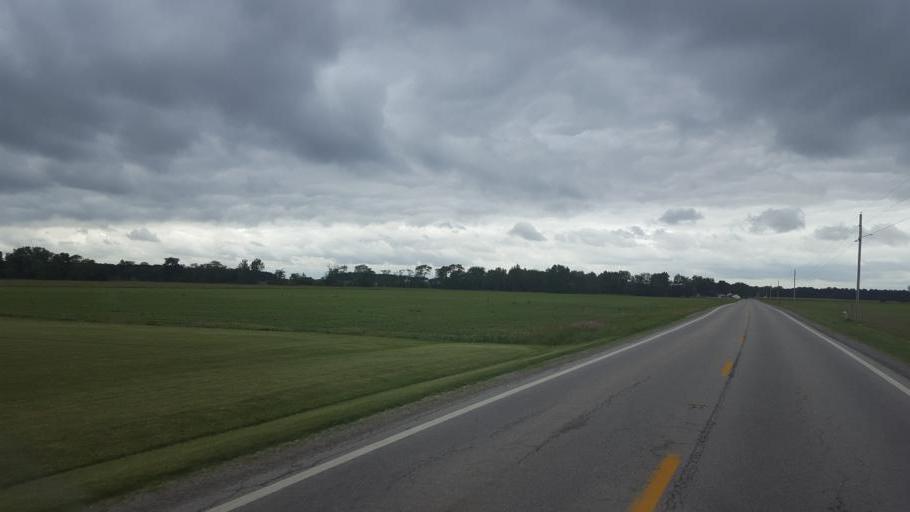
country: US
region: Ohio
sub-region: Marion County
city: Marion
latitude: 40.6639
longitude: -83.1448
